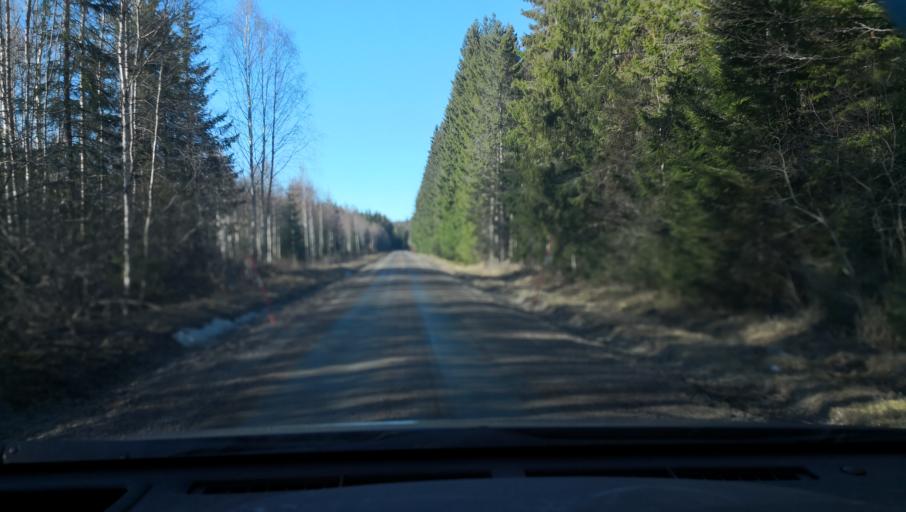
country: SE
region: Vaestmanland
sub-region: Sala Kommun
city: Sala
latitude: 60.1373
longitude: 16.6493
